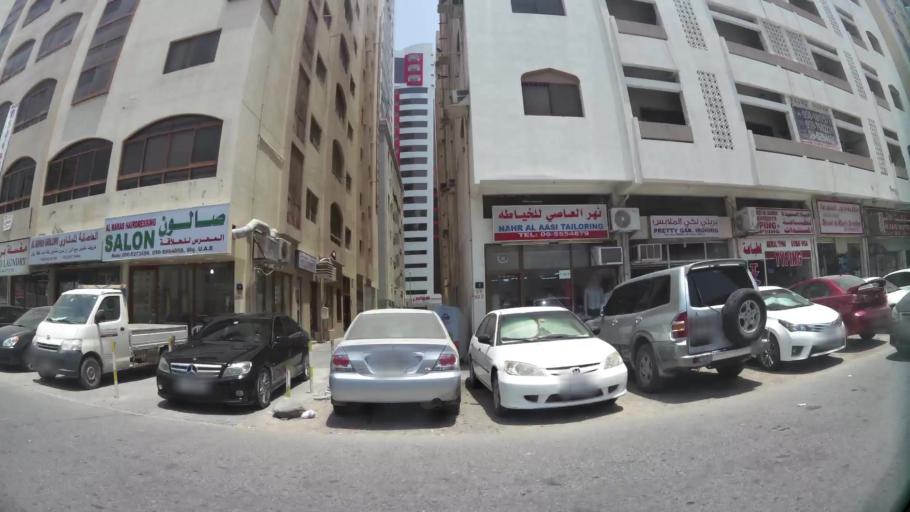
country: AE
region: Ash Shariqah
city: Sharjah
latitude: 25.3182
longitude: 55.3824
